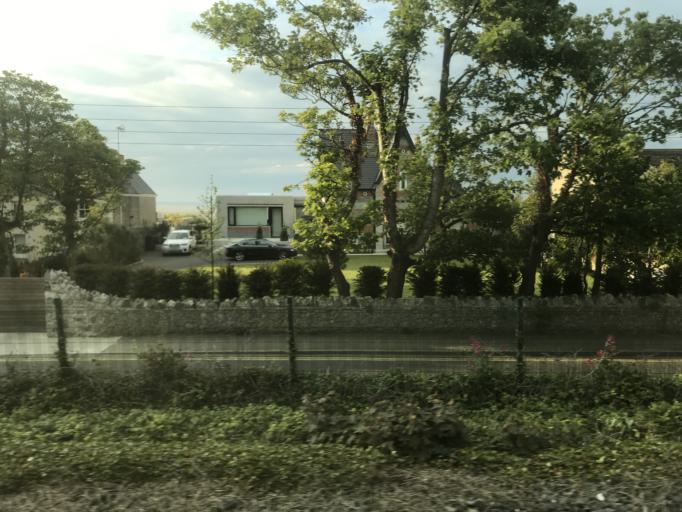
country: IE
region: Leinster
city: Sutton
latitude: 53.3915
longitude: -6.0985
